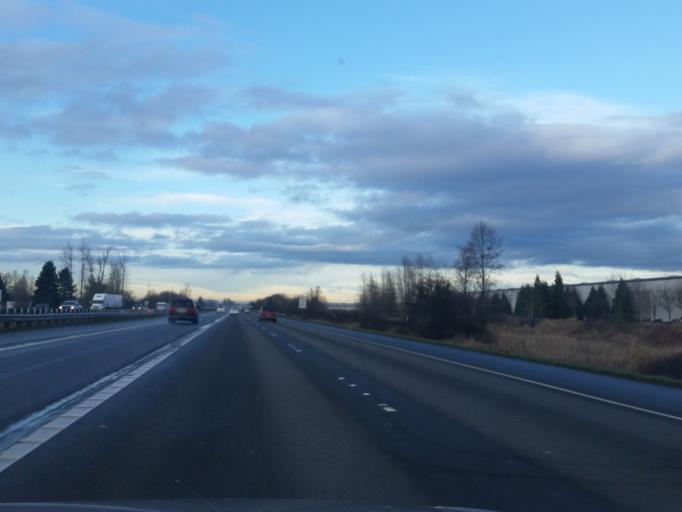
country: US
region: Washington
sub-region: King County
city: Lakeland North
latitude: 47.3406
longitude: -122.2446
